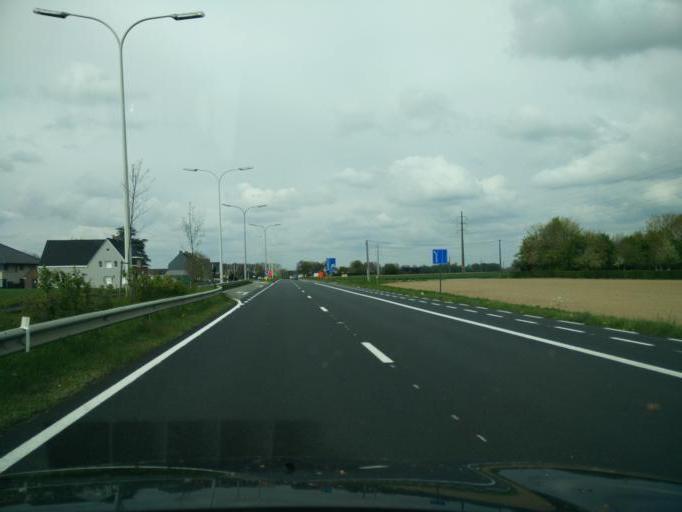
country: BE
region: Flanders
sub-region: Provincie Oost-Vlaanderen
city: Oudenaarde
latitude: 50.8879
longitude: 3.6161
